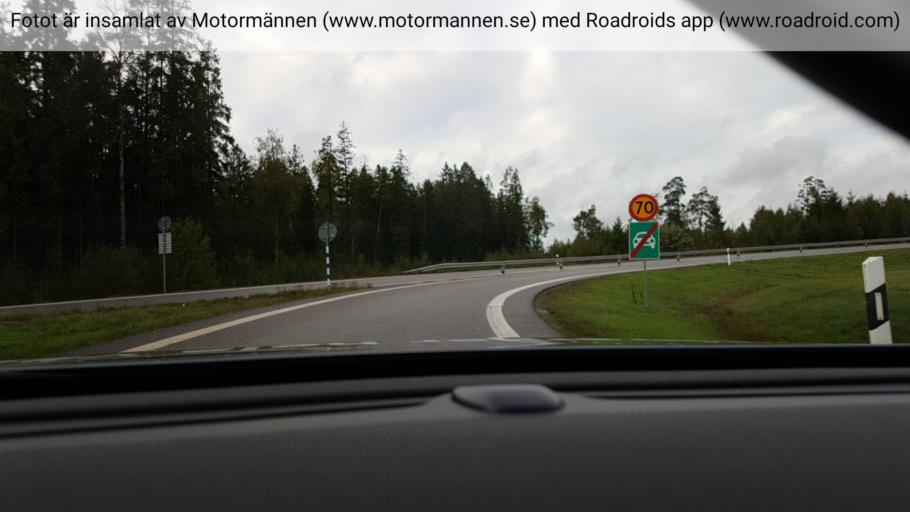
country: SE
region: Vaestra Goetaland
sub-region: Trollhattan
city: Trollhattan
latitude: 58.3383
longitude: 12.2358
